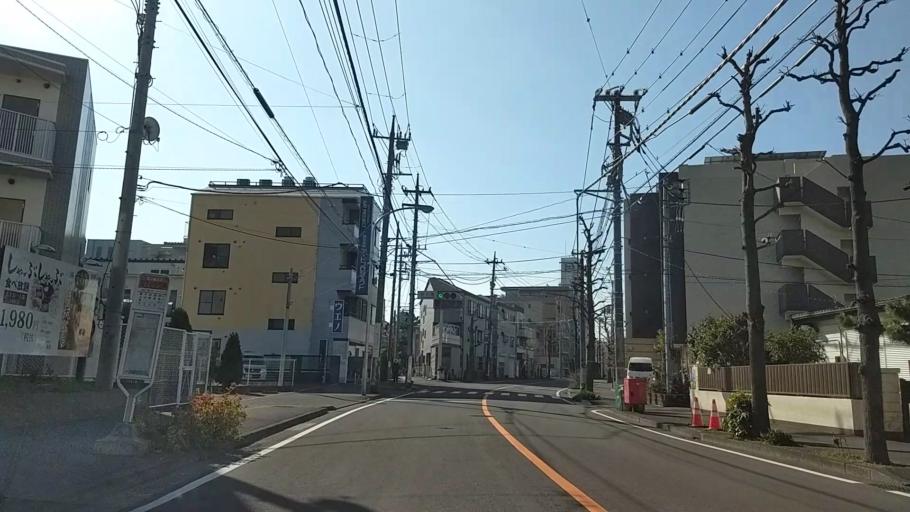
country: JP
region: Kanagawa
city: Yokohama
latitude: 35.3895
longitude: 139.6016
